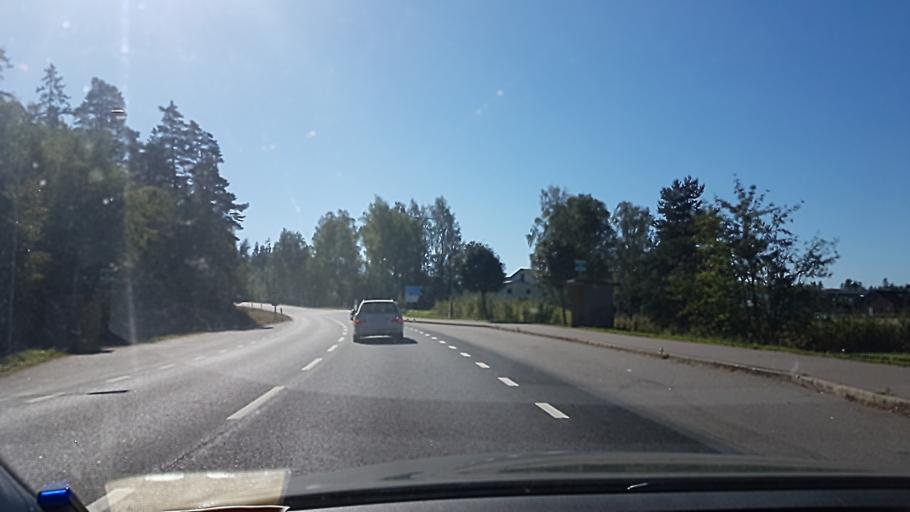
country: SE
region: Kronoberg
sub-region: Lessebo Kommun
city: Lessebo
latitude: 56.7447
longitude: 15.2692
